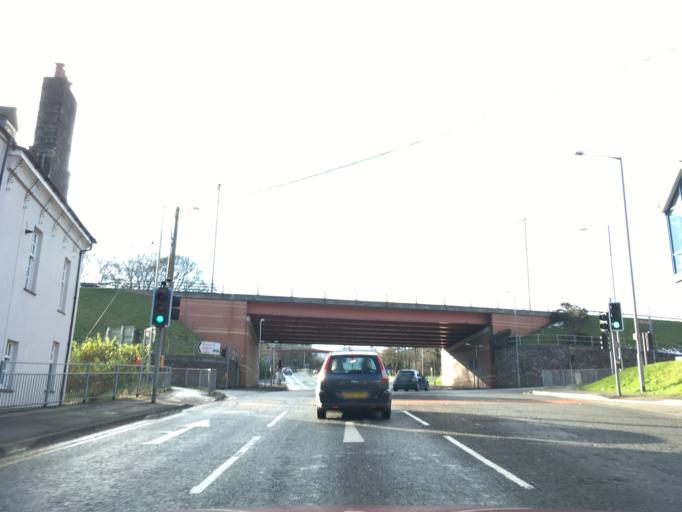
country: GB
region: Wales
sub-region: Torfaen County Borough
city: Pontypool
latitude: 51.6981
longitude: -3.0290
